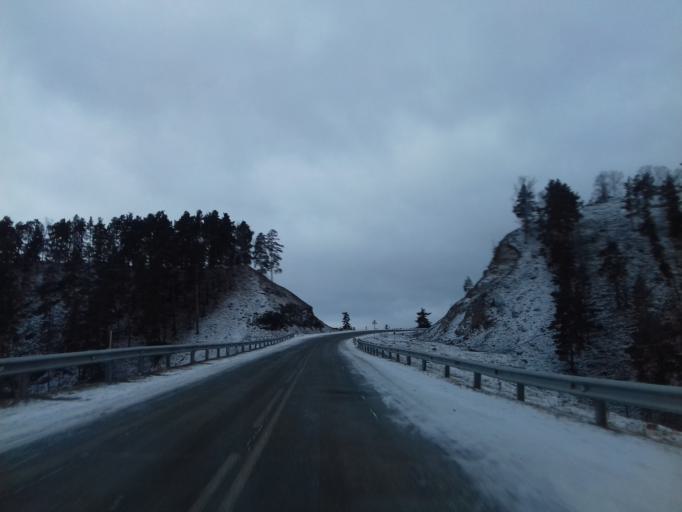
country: RU
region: Bashkortostan
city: Starosubkhangulovo
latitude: 53.2822
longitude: 57.5465
